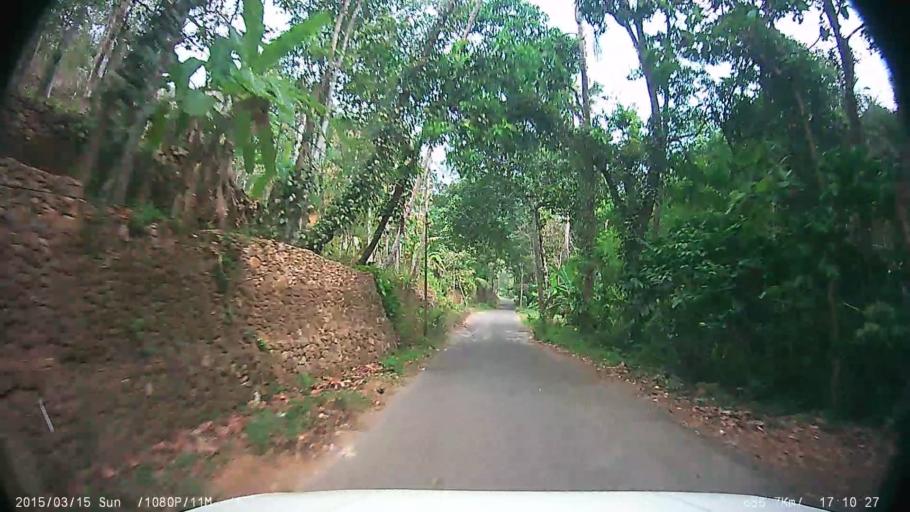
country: IN
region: Kerala
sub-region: Kottayam
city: Palackattumala
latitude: 9.8605
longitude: 76.6746
